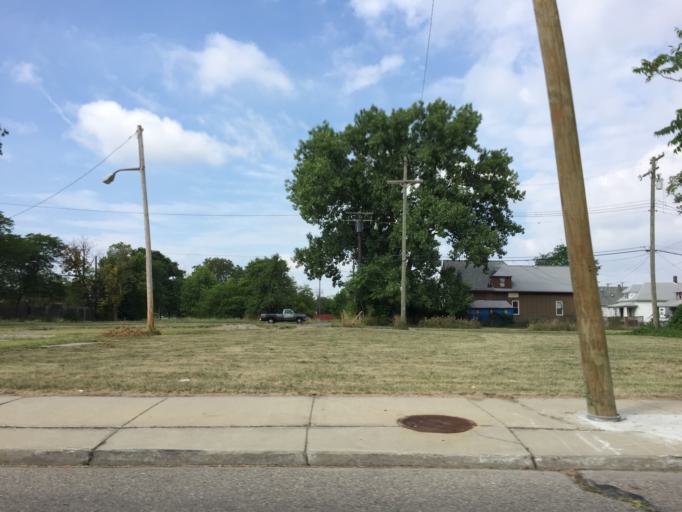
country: US
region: Michigan
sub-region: Wayne County
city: Detroit
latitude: 42.3602
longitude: -83.0373
